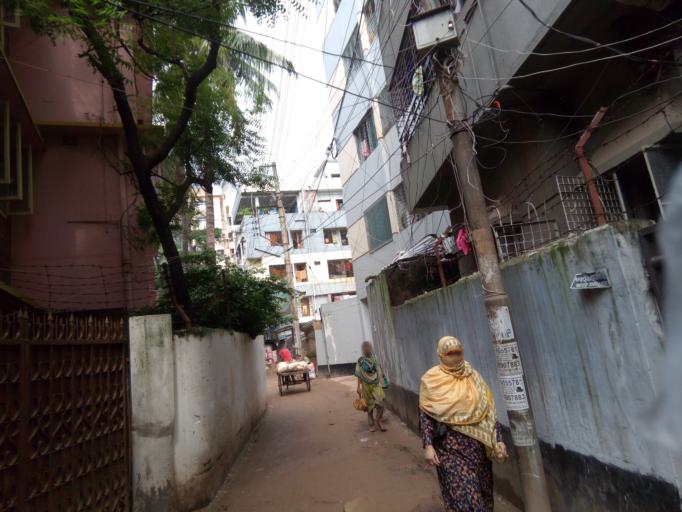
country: BD
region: Dhaka
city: Azimpur
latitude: 23.7417
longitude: 90.3658
